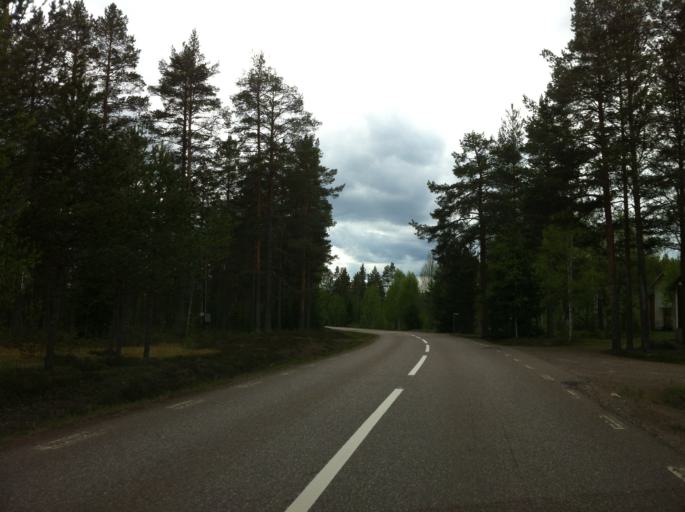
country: NO
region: Hedmark
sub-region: Trysil
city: Innbygda
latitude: 61.4363
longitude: 13.0998
